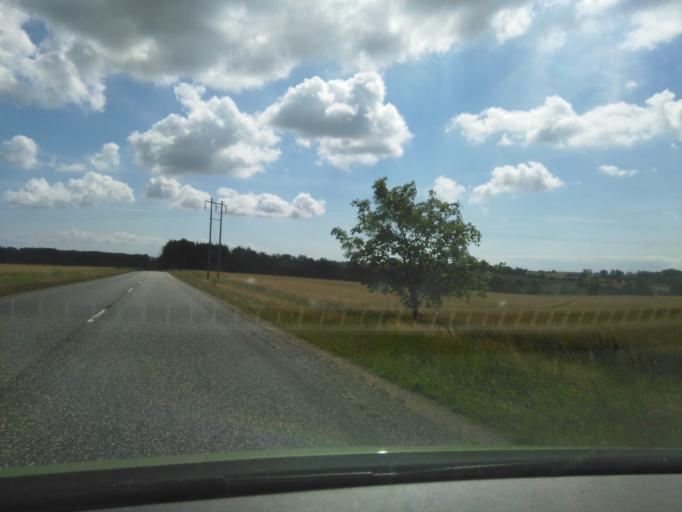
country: DK
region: Central Jutland
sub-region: Odder Kommune
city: Odder
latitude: 55.9653
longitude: 10.0954
